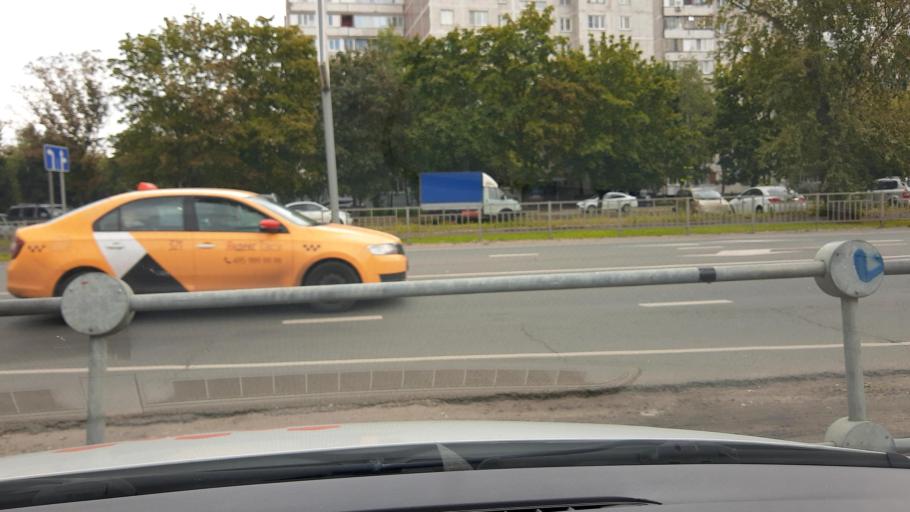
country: RU
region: Moskovskaya
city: Elektrostal'
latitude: 55.7766
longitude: 38.4333
